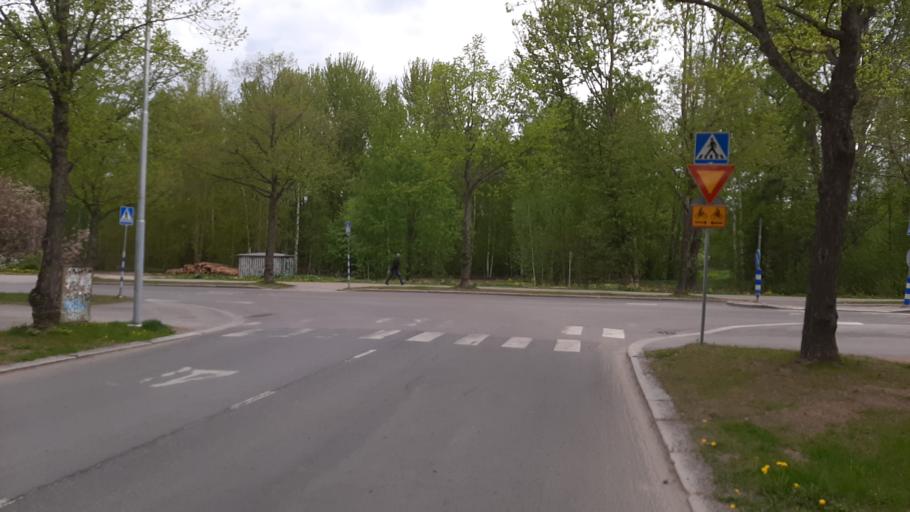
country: FI
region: Pirkanmaa
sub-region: Tampere
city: Tampere
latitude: 61.4837
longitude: 23.8007
